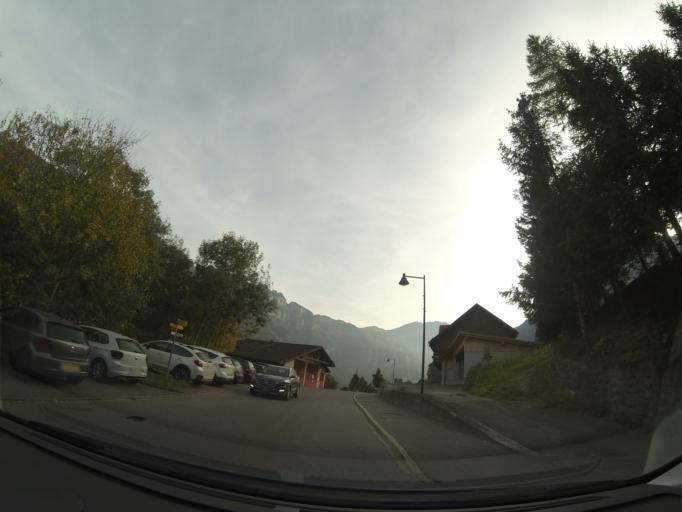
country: CH
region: Saint Gallen
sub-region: Wahlkreis Sarganserland
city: Bad Ragaz
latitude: 46.9683
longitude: 9.4784
